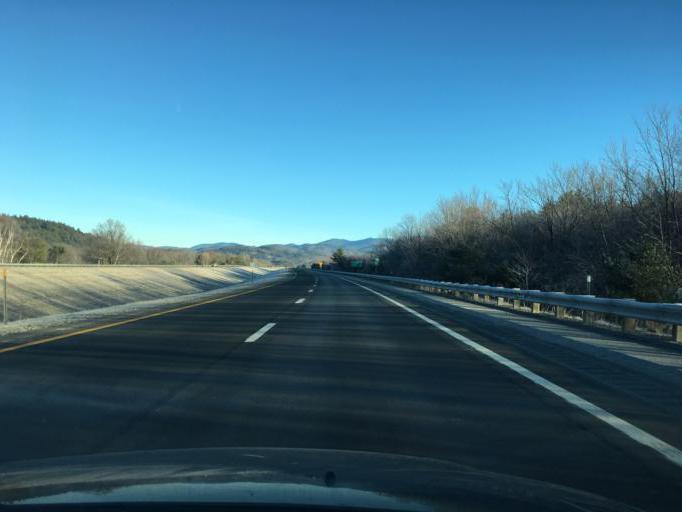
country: US
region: New Hampshire
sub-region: Grafton County
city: Plymouth
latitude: 43.8203
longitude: -71.6601
